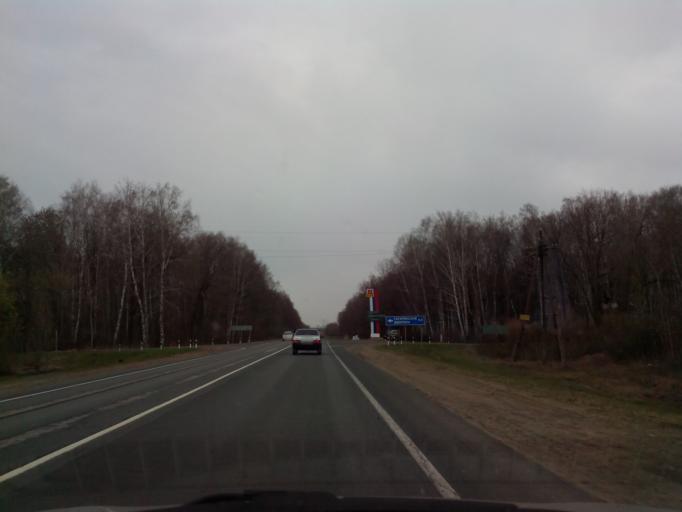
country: RU
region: Tambov
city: Michurinsk
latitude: 53.0715
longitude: 40.4296
